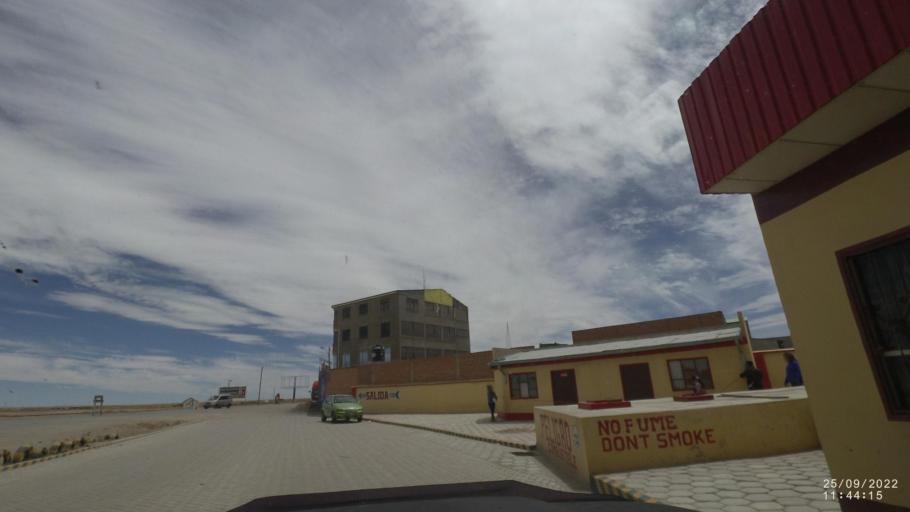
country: BO
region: Oruro
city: Challapata
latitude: -18.8930
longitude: -66.7789
